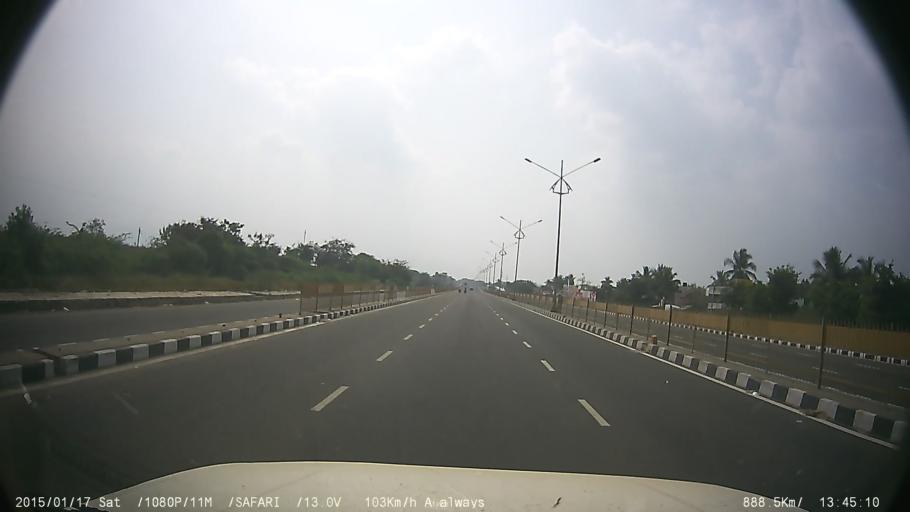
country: IN
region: Tamil Nadu
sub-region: Vellore
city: Vellore
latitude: 12.9222
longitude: 79.0978
